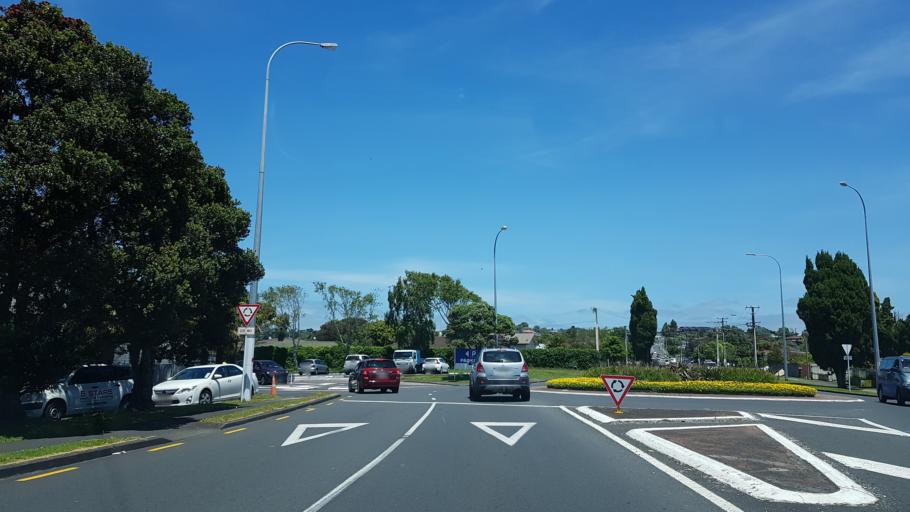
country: NZ
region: Auckland
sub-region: Auckland
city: Waitakere
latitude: -36.9092
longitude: 174.6631
